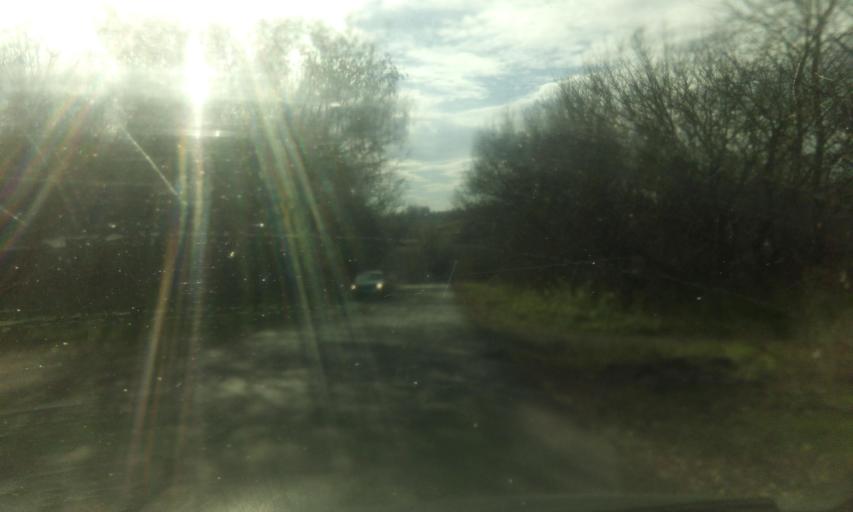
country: RU
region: Tula
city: Dubovka
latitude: 53.9505
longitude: 38.0285
